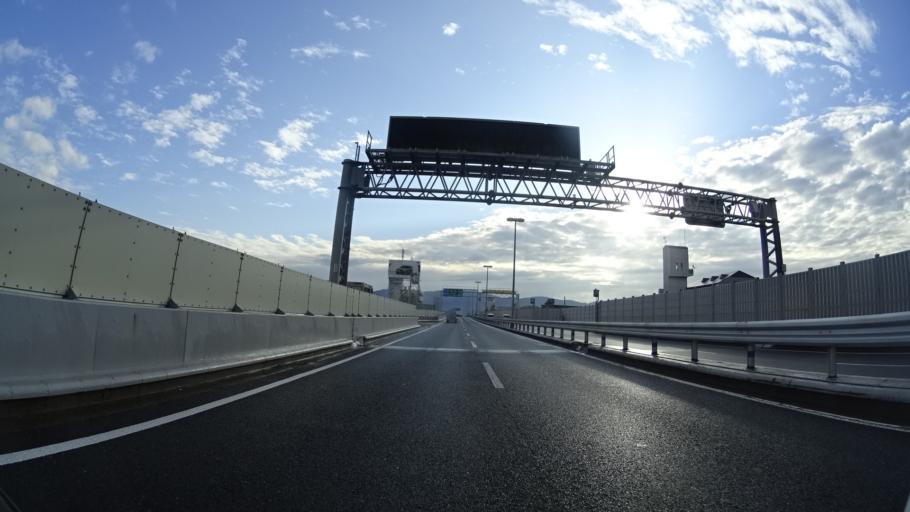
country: JP
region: Osaka
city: Daitocho
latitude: 34.6789
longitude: 135.5786
